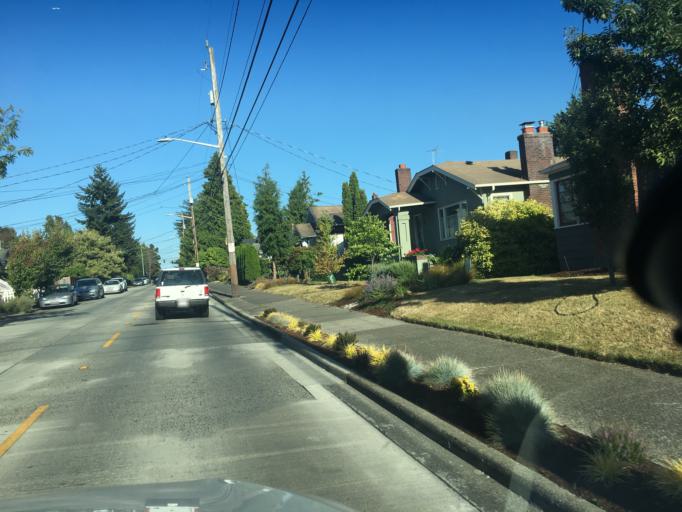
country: US
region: Washington
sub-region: King County
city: Shoreline
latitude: 47.6869
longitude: -122.3526
